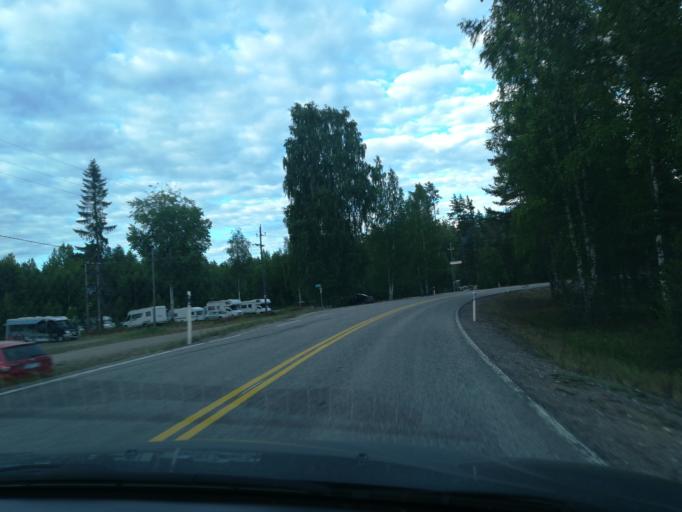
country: FI
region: Southern Savonia
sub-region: Mikkeli
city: Puumala
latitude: 61.5635
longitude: 27.9910
